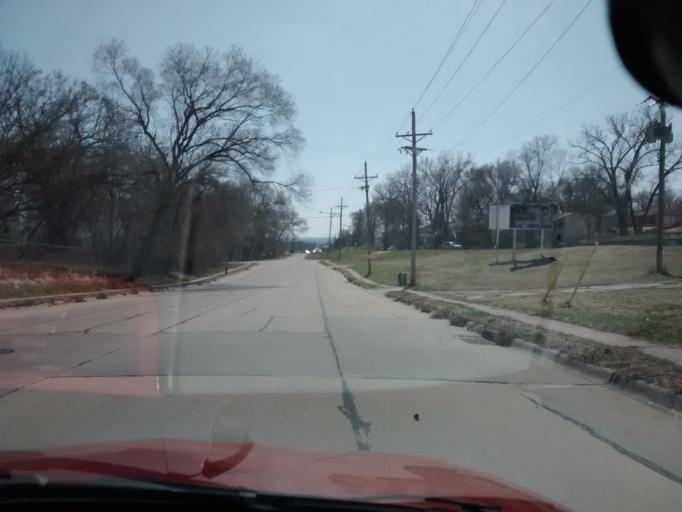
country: US
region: Nebraska
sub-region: Sarpy County
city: Bellevue
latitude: 41.1401
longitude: -95.9074
